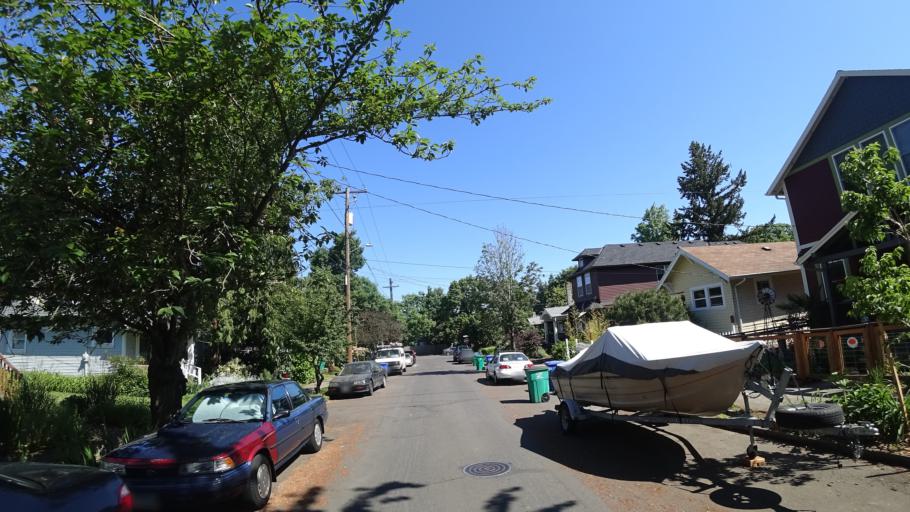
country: US
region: Oregon
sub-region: Multnomah County
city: Portland
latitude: 45.5621
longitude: -122.6468
